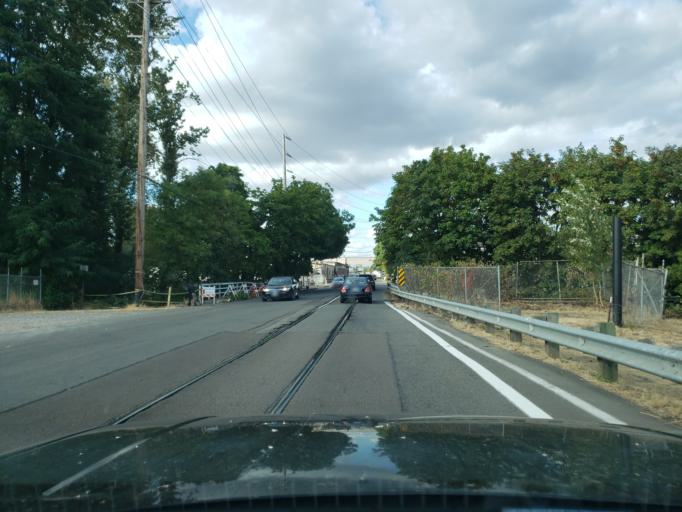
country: US
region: Oregon
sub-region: Marion County
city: Salem
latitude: 44.9504
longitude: -123.0373
